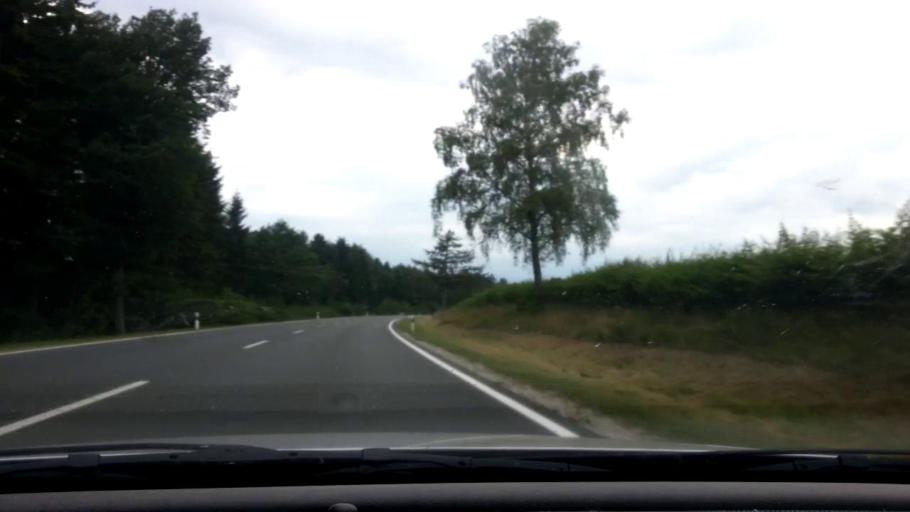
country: DE
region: Bavaria
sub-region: Upper Palatinate
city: Erbendorf
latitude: 49.8396
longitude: 12.0080
